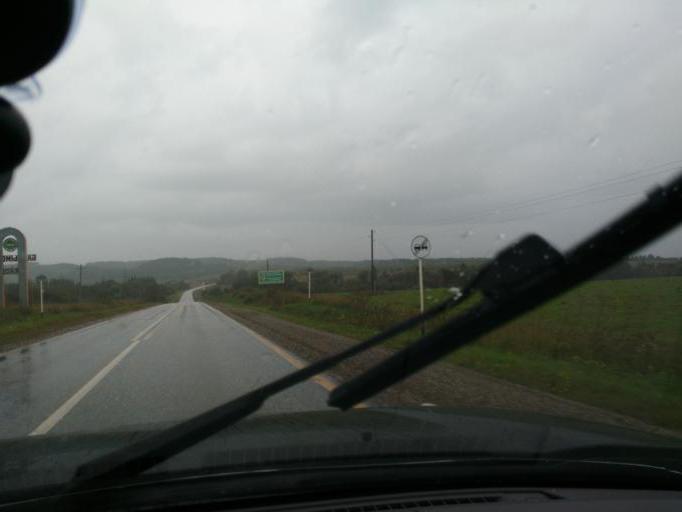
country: RU
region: Perm
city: Barda
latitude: 57.1037
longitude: 55.5269
